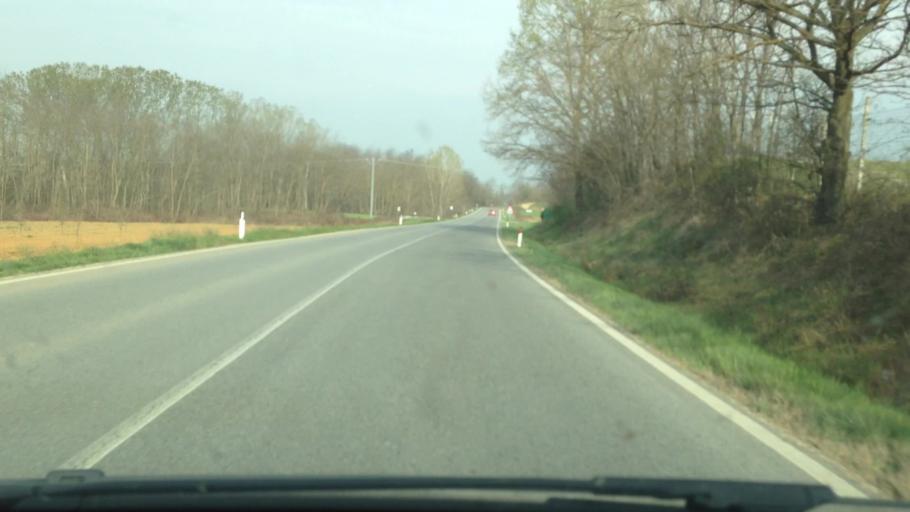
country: IT
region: Piedmont
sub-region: Provincia di Cuneo
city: Monta
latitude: 44.8290
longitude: 7.9310
